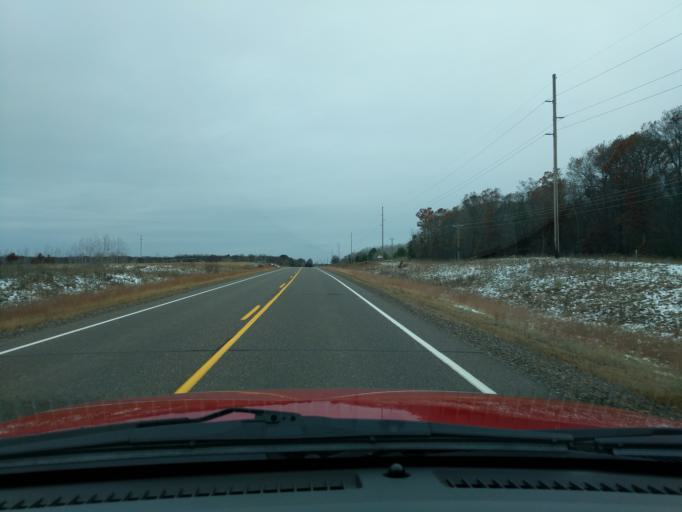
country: US
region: Wisconsin
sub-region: Washburn County
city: Shell Lake
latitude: 45.8158
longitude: -92.1170
